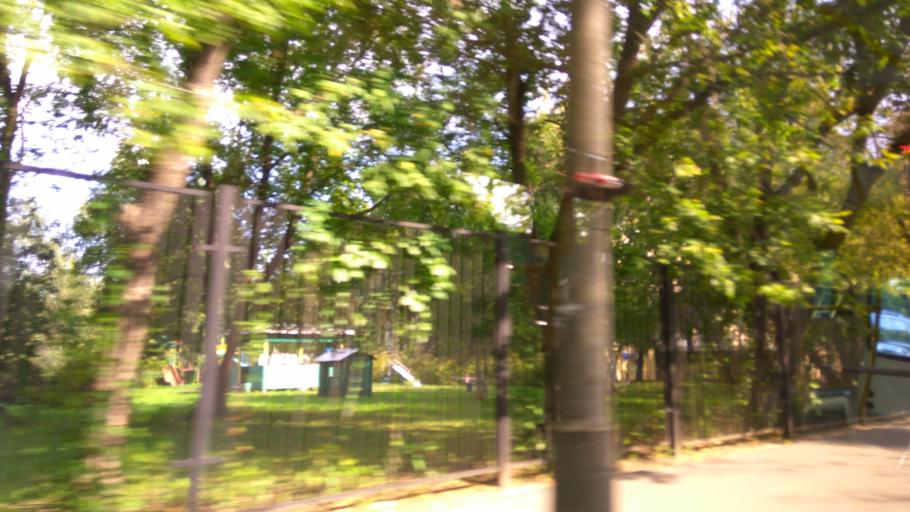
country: RU
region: Moscow
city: Lefortovo
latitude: 55.7687
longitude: 37.7388
